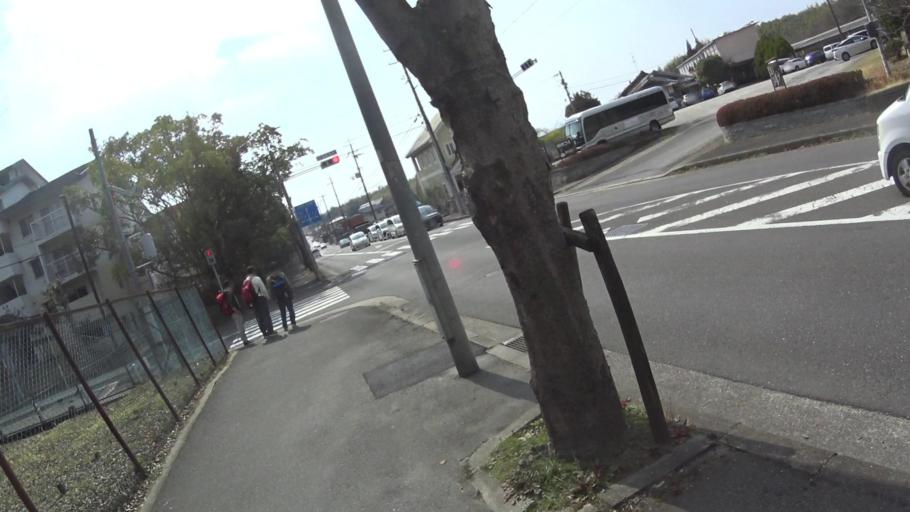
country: JP
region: Nara
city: Nara-shi
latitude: 34.7121
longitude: 135.8319
